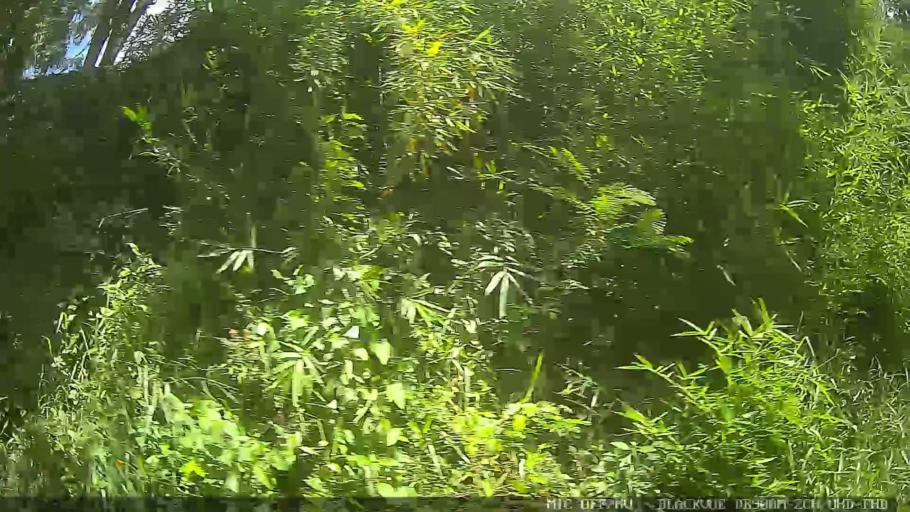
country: BR
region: Minas Gerais
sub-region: Extrema
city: Extrema
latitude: -22.8653
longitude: -46.2856
